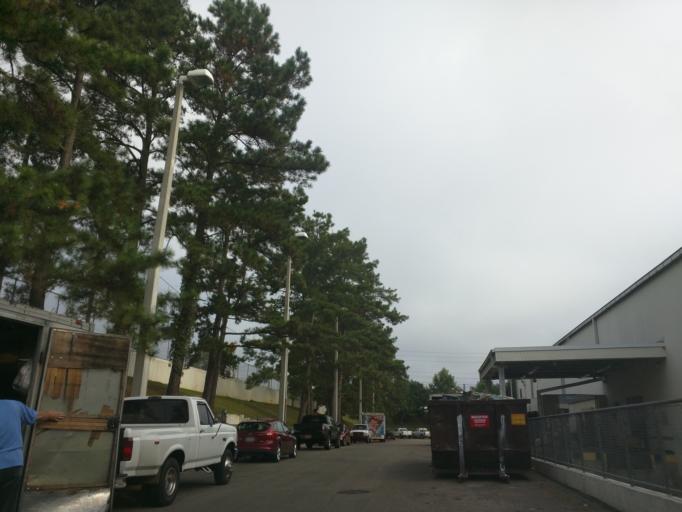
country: US
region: Florida
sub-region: Leon County
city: Tallahassee
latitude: 30.4624
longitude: -84.2852
